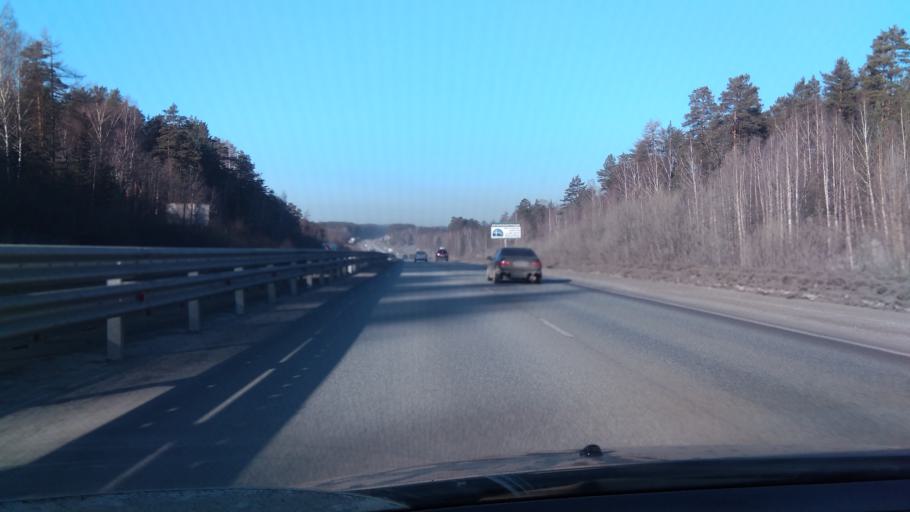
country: RU
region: Sverdlovsk
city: Severka
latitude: 56.8319
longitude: 60.3771
